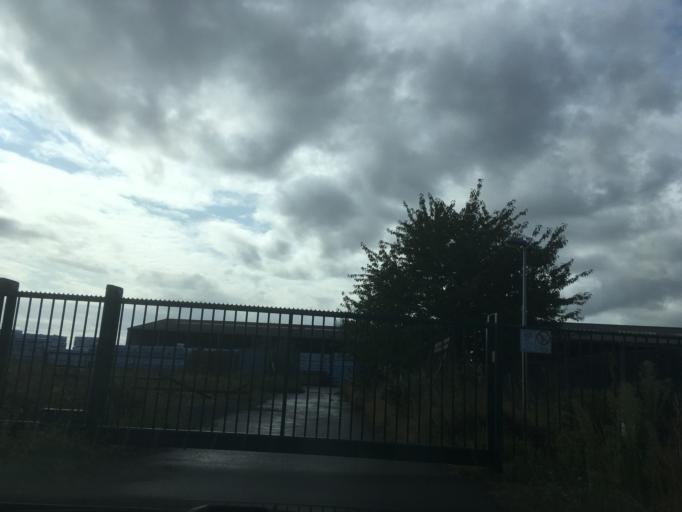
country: BE
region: Flanders
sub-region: Provincie West-Vlaanderen
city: Hooglede
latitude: 50.9919
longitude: 3.1202
